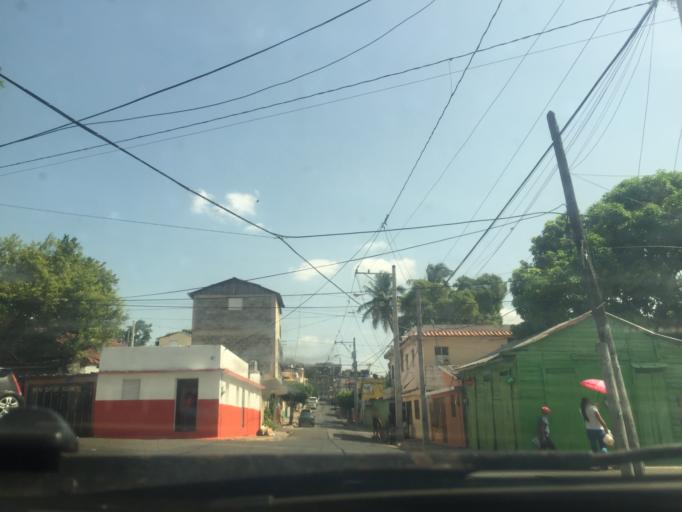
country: DO
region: Santiago
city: Santiago de los Caballeros
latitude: 19.4596
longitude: -70.7054
